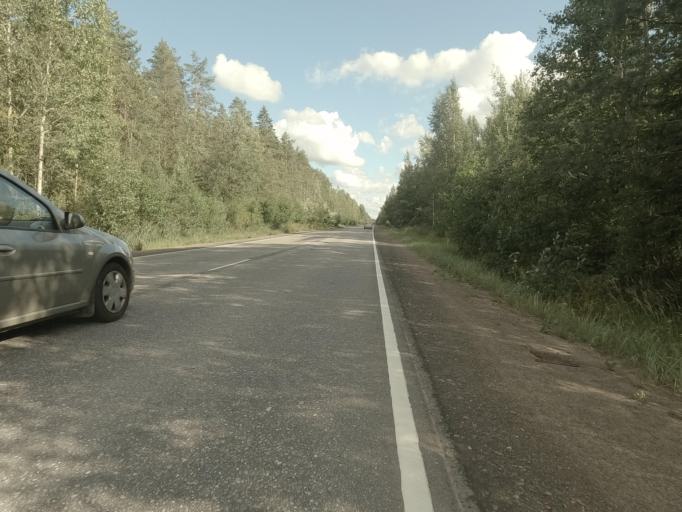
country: RU
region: Leningrad
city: Shcheglovo
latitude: 60.0001
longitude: 30.8713
